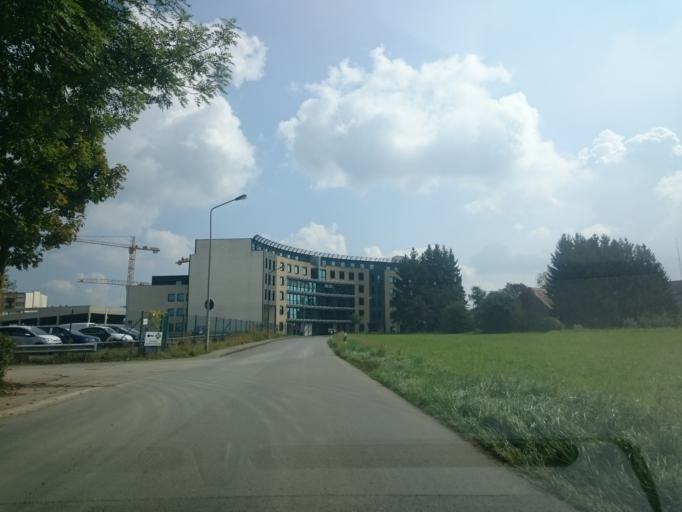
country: LU
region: Luxembourg
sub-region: Canton de Luxembourg
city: Luxembourg
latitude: 49.5904
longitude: 6.1139
